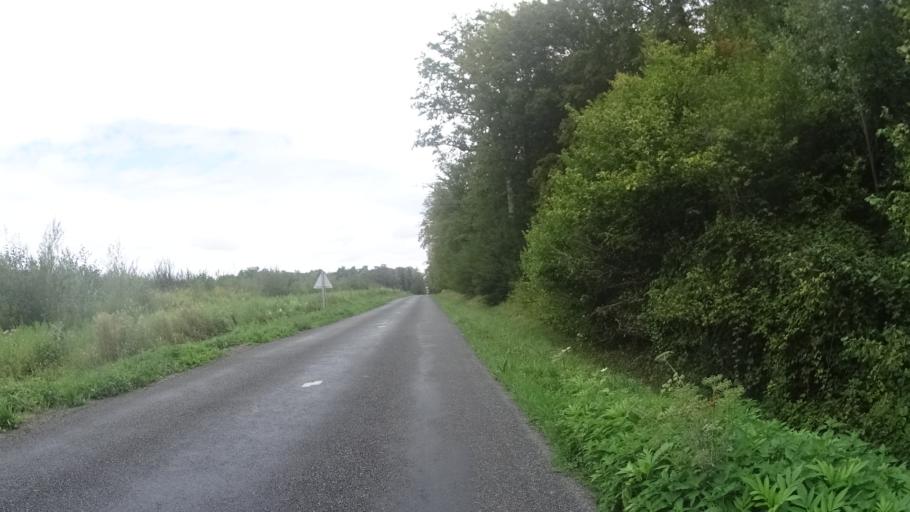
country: FR
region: Picardie
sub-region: Departement de l'Oise
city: Chiry-Ourscamp
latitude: 49.5429
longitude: 2.9823
